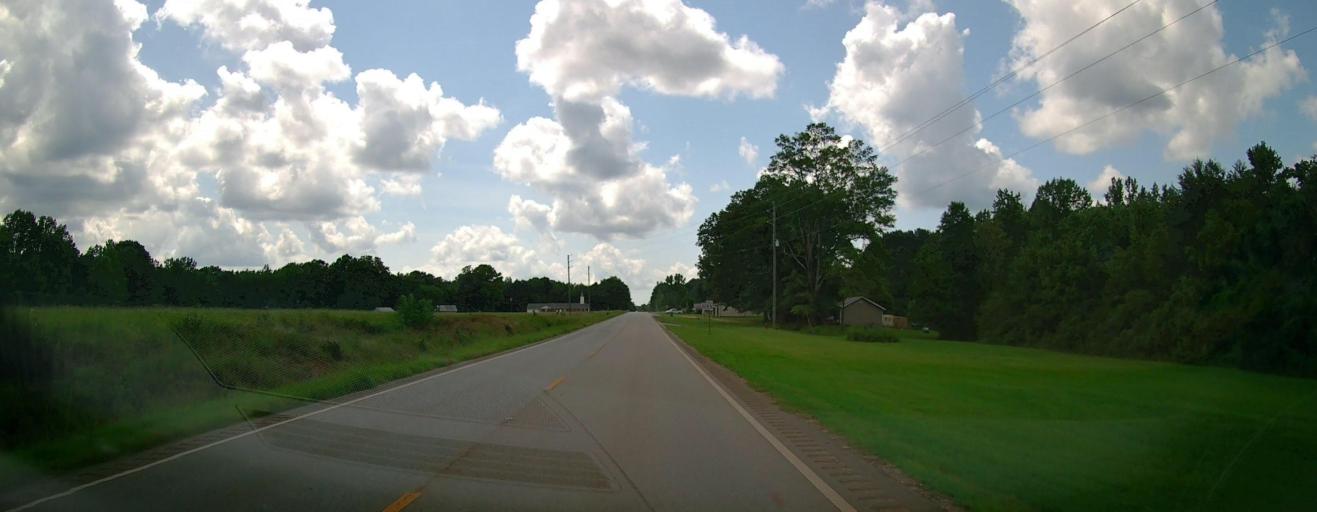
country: US
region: Georgia
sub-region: Carroll County
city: Bowdon
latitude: 33.5637
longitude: -85.4296
